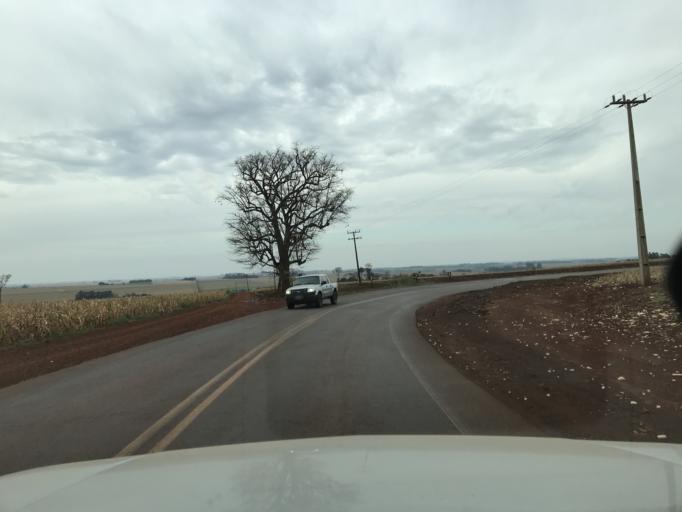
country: BR
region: Parana
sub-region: Palotina
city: Palotina
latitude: -24.4204
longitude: -53.8834
